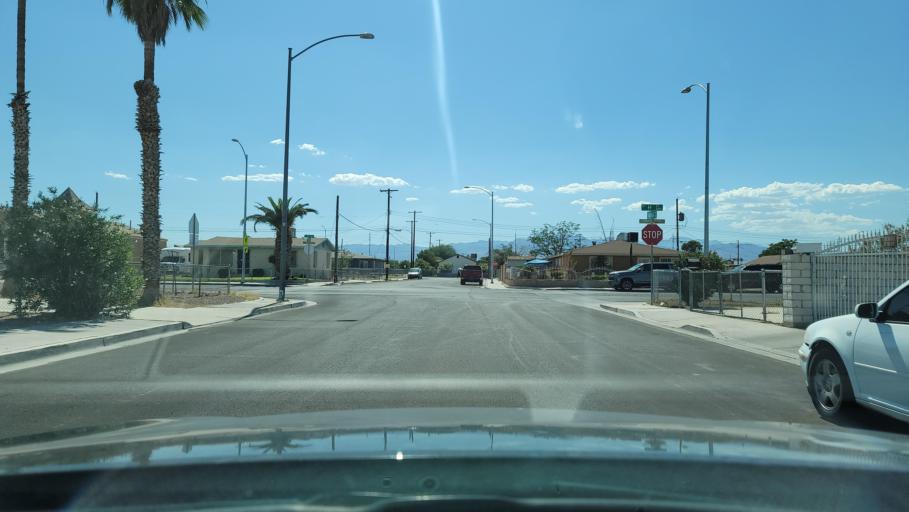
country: US
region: Nevada
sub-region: Clark County
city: Las Vegas
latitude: 36.1839
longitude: -115.1514
